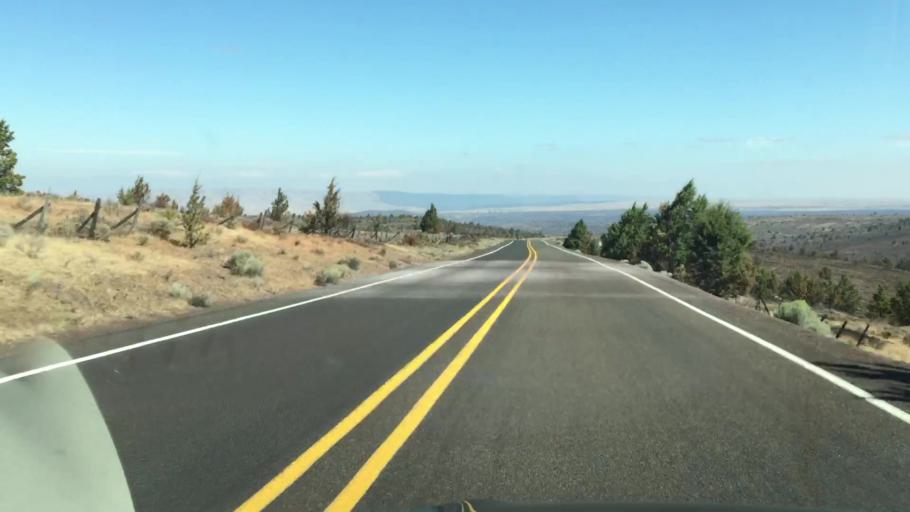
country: US
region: Oregon
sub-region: Jefferson County
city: Warm Springs
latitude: 45.0681
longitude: -121.0234
